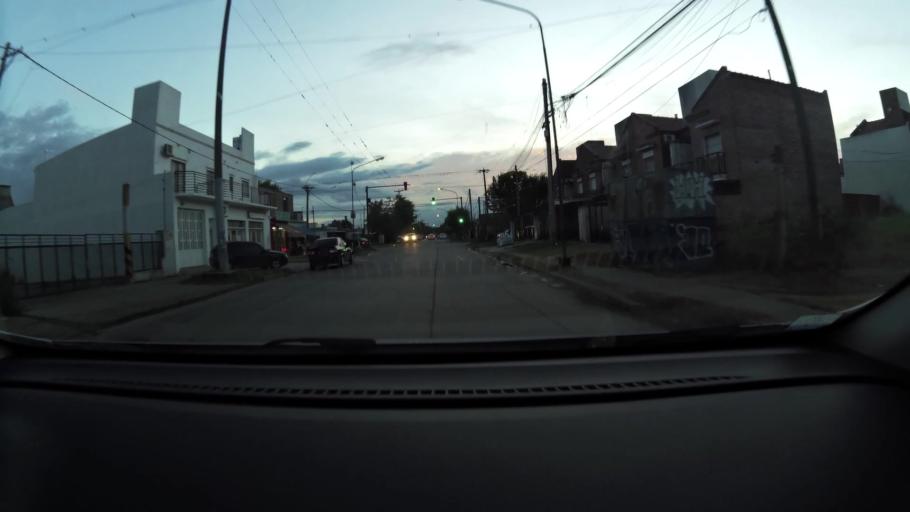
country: AR
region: Buenos Aires
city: San Nicolas de los Arroyos
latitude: -33.3493
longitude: -60.1957
